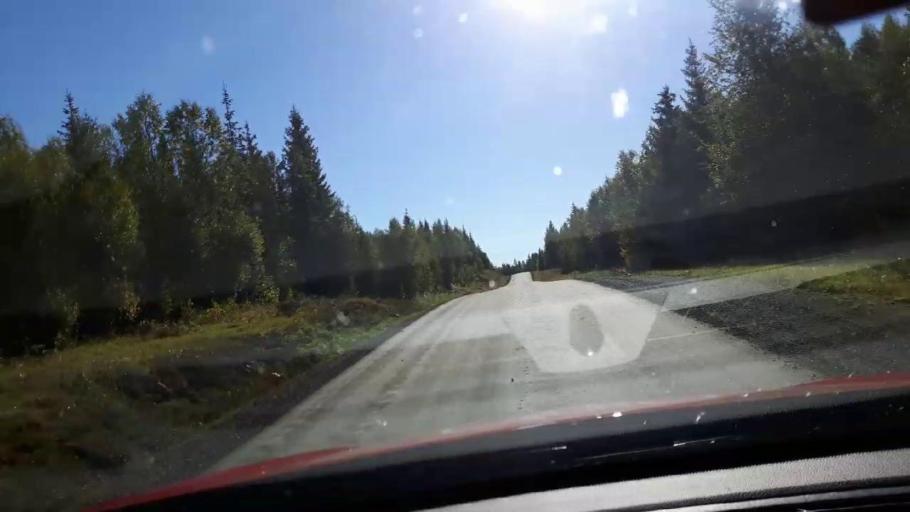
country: NO
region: Nord-Trondelag
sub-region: Lierne
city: Sandvika
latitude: 64.6010
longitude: 13.9710
